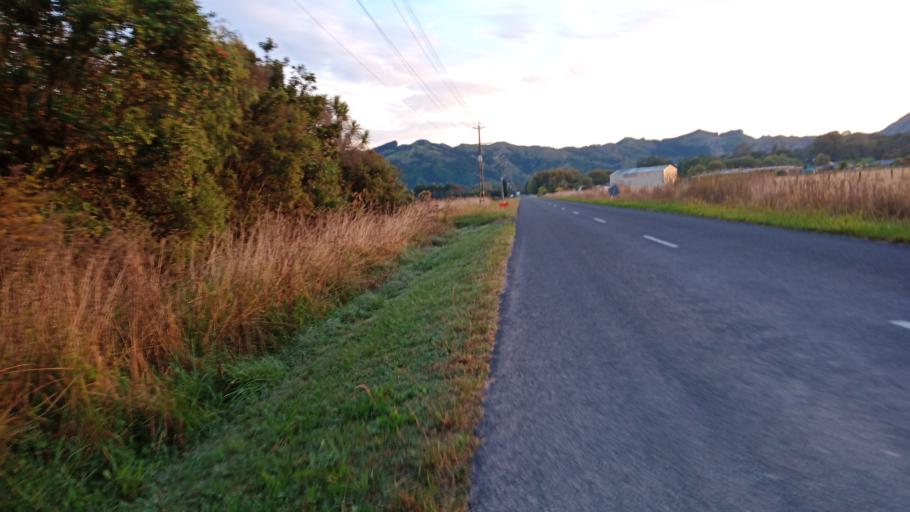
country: NZ
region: Gisborne
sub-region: Gisborne District
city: Gisborne
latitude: -38.6277
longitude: 177.9765
